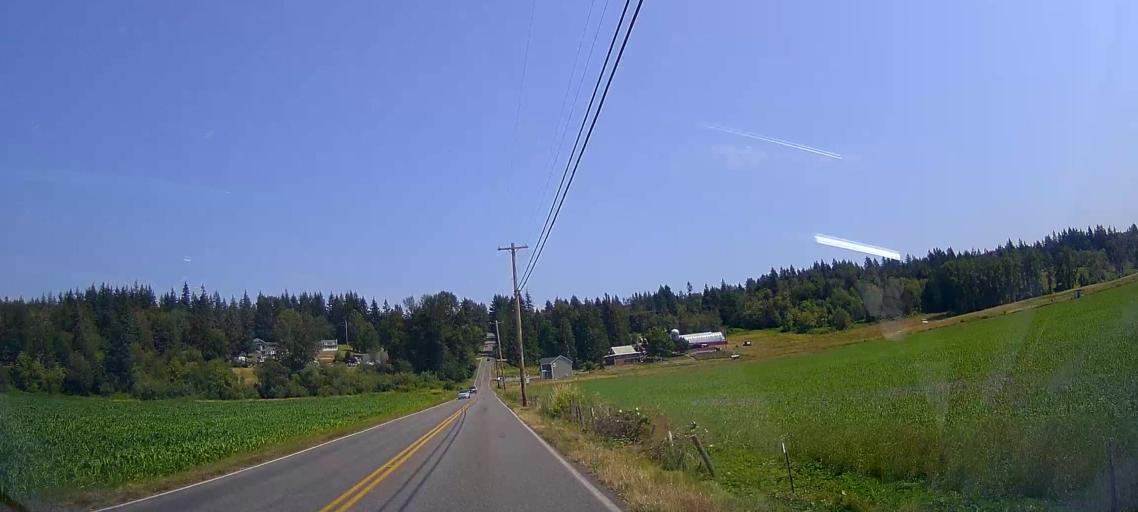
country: US
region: Washington
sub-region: Snohomish County
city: Sisco Heights
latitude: 48.0920
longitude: -122.1336
